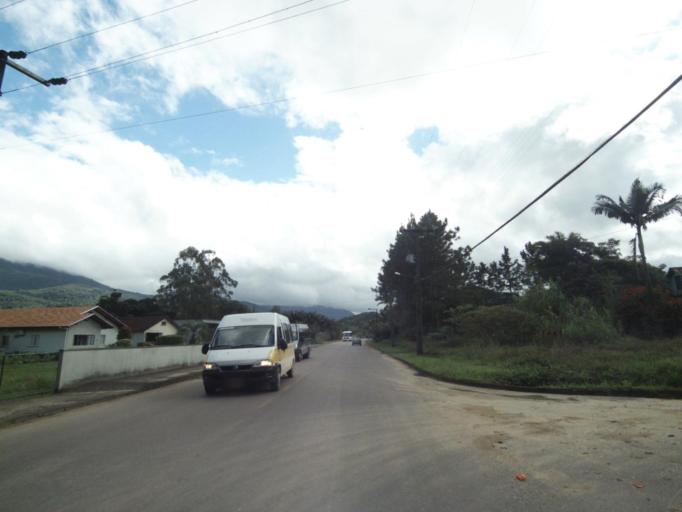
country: BR
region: Santa Catarina
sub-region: Pomerode
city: Pomerode
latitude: -26.6873
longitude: -49.1752
